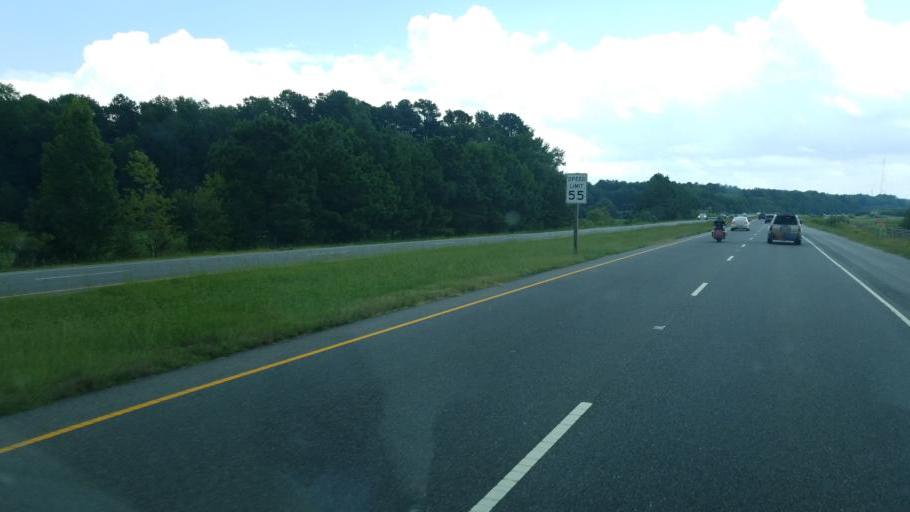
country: US
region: North Carolina
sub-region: Currituck County
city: Moyock
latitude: 36.6490
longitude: -76.2242
